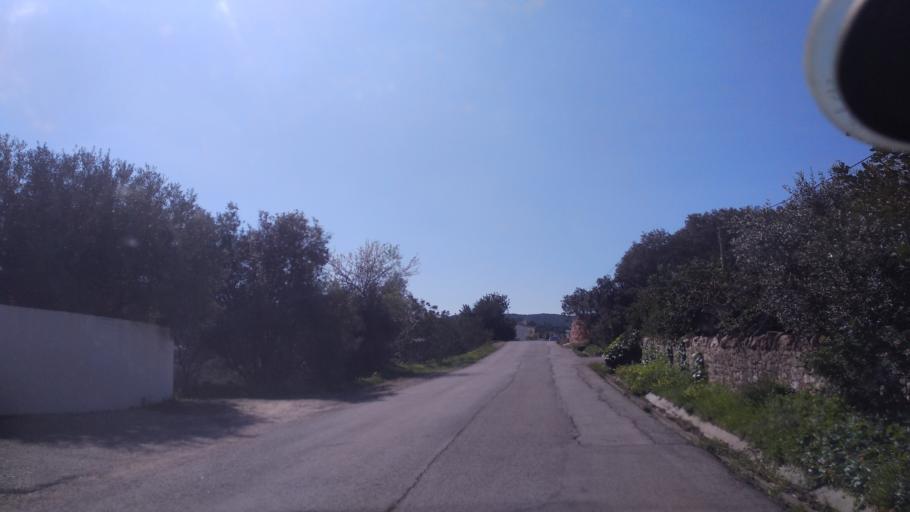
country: PT
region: Faro
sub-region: Faro
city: Santa Barbara de Nexe
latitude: 37.1137
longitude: -7.9322
